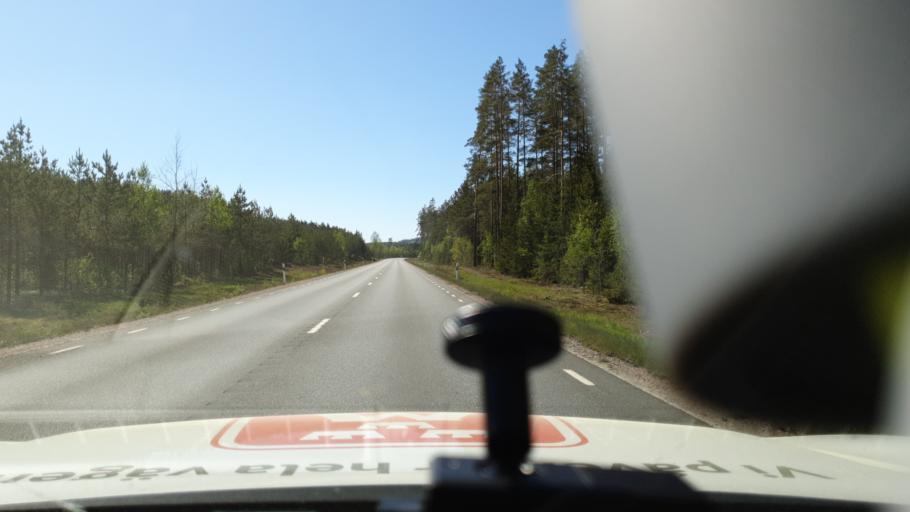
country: SE
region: Kalmar
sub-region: Hultsfreds Kommun
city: Virserum
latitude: 57.3968
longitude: 15.4345
